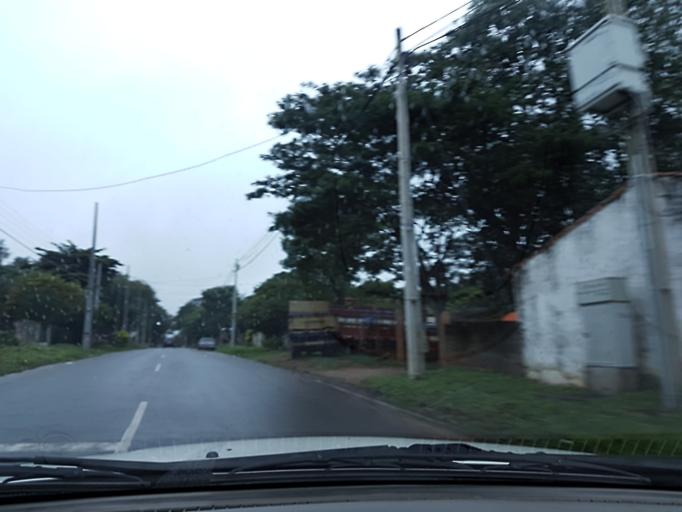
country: PY
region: Central
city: Colonia Mariano Roque Alonso
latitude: -25.2166
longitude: -57.5427
